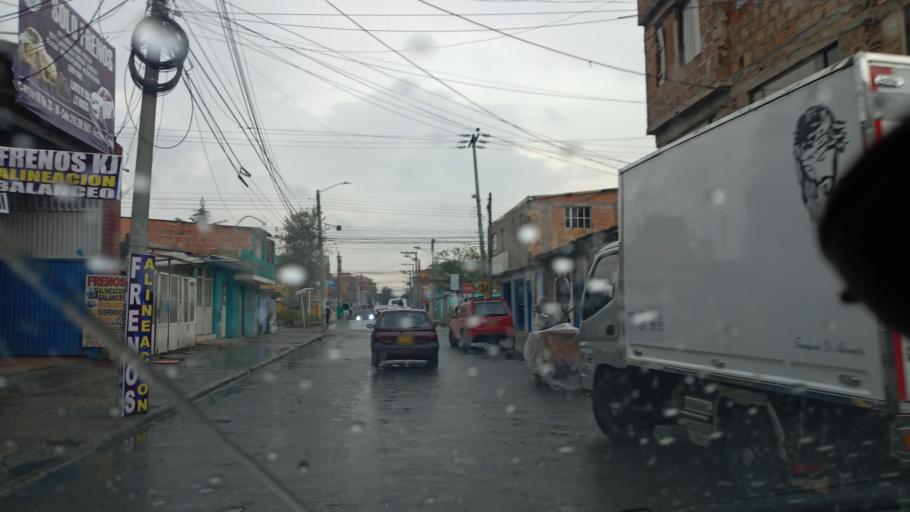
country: CO
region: Cundinamarca
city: Funza
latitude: 4.6809
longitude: -74.1442
